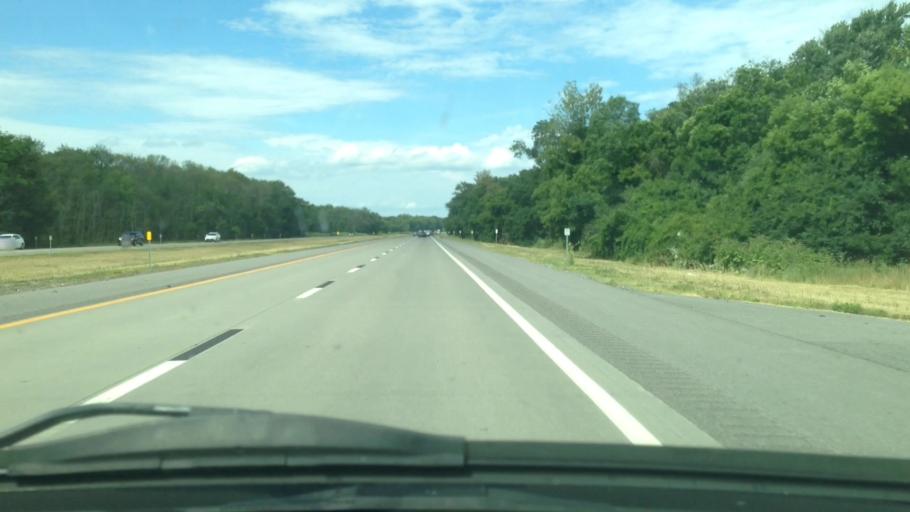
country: US
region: New York
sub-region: Cayuga County
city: Weedsport
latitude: 43.0696
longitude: -76.5244
